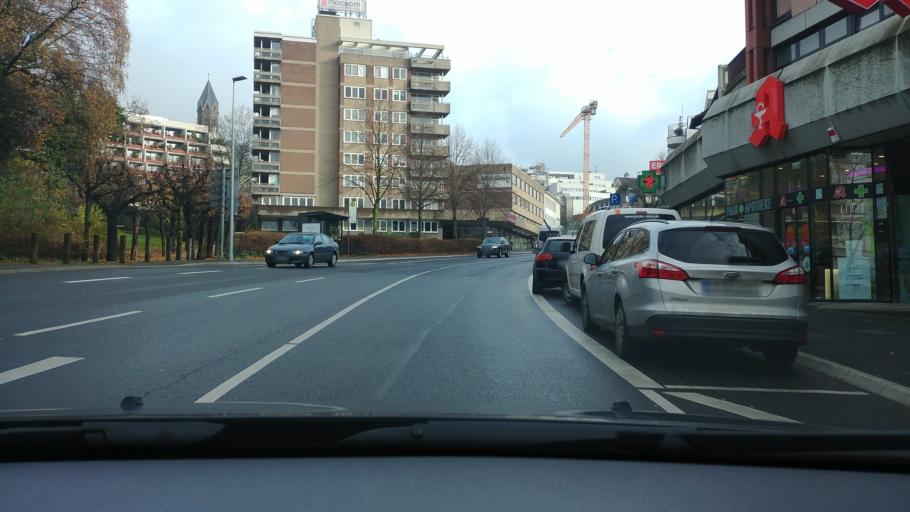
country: DE
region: North Rhine-Westphalia
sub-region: Regierungsbezirk Koln
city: Bergisch Gladbach
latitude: 50.9652
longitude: 7.1543
